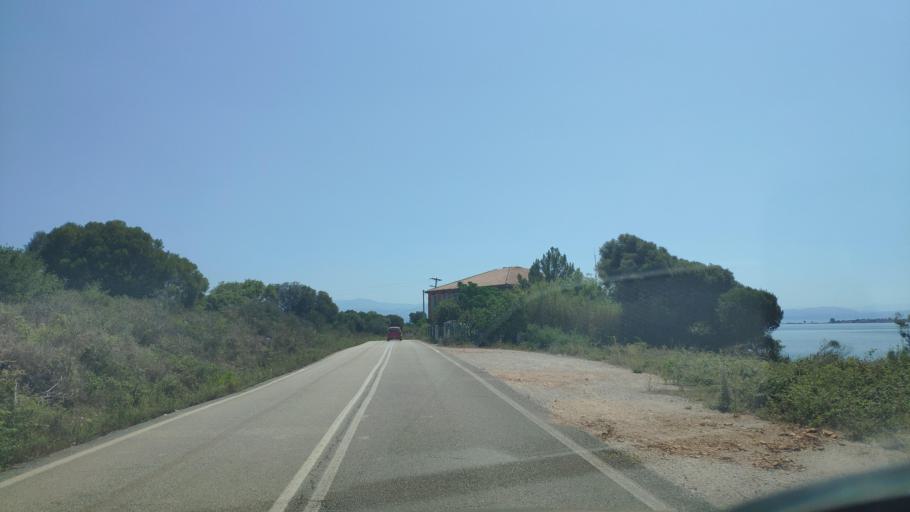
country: GR
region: Epirus
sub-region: Nomos Artas
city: Aneza
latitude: 39.0312
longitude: 20.8668
